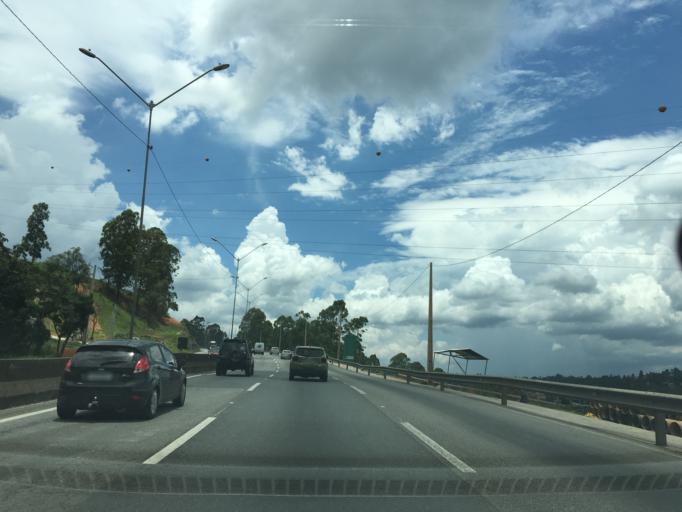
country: BR
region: Sao Paulo
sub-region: Mairipora
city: Mairipora
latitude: -23.3064
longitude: -46.5756
